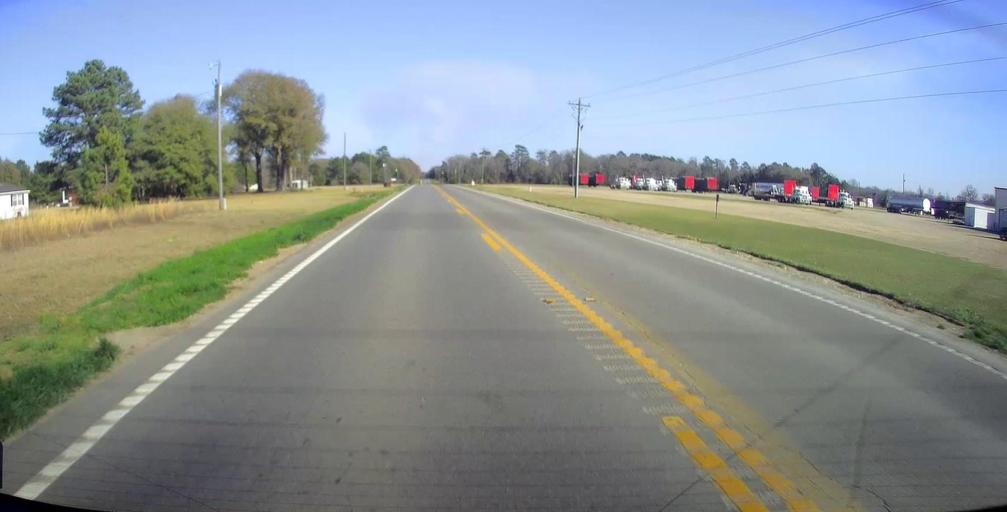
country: US
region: Georgia
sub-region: Macon County
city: Oglethorpe
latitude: 32.3339
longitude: -84.1110
